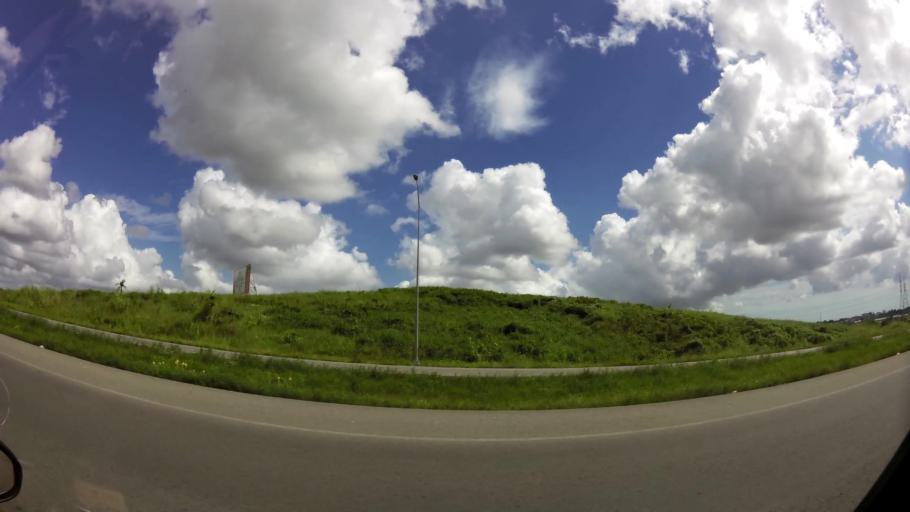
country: TT
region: Penal/Debe
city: Debe
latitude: 10.2254
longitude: -61.4502
